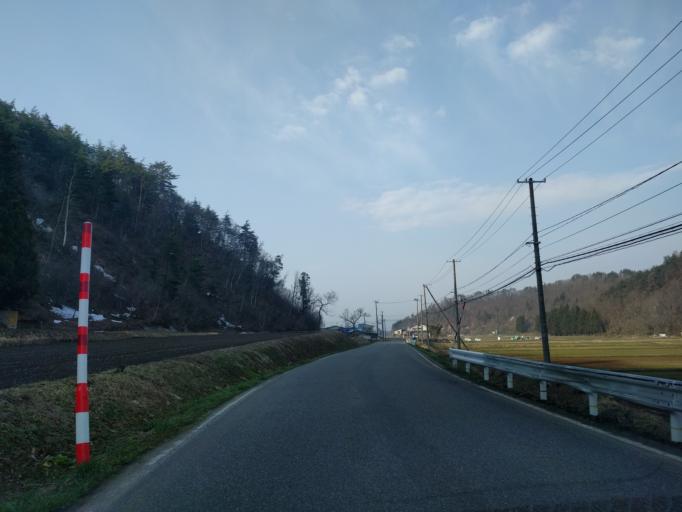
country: JP
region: Fukushima
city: Kitakata
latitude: 37.6911
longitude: 139.9078
